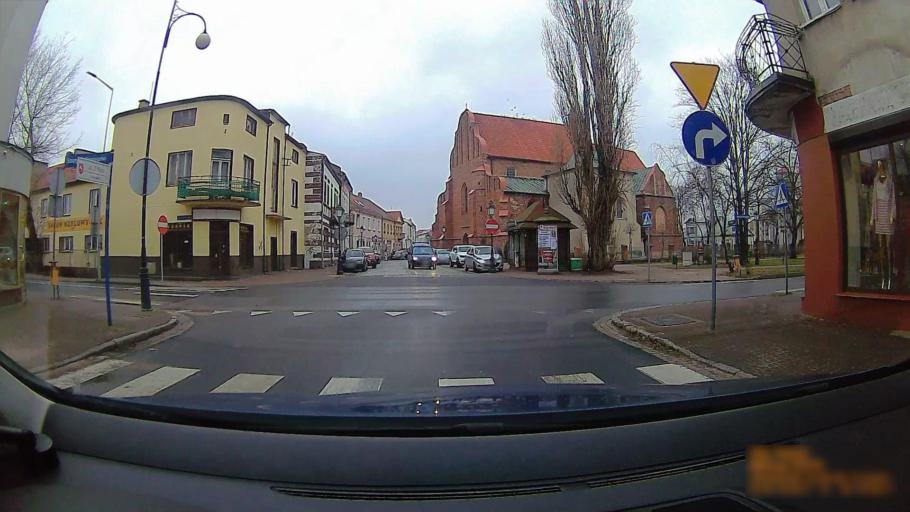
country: PL
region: Greater Poland Voivodeship
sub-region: Konin
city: Konin
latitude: 52.2073
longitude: 18.2545
